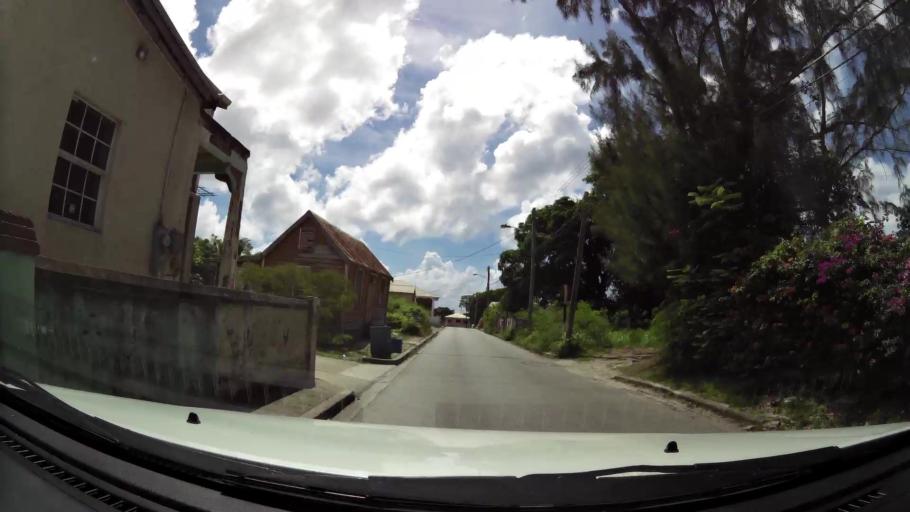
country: BB
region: Saint Michael
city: Bridgetown
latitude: 13.1269
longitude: -59.6250
